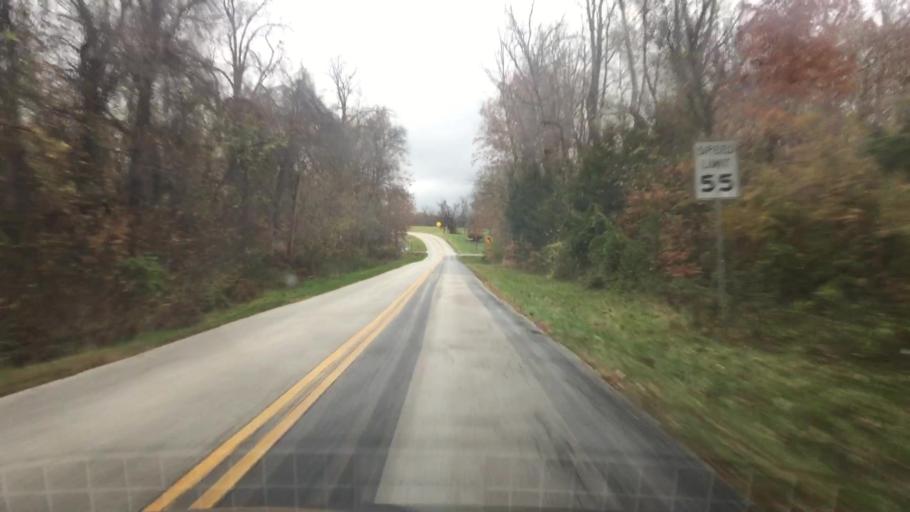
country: US
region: Missouri
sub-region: Boone County
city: Columbia
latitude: 38.9132
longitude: -92.4700
